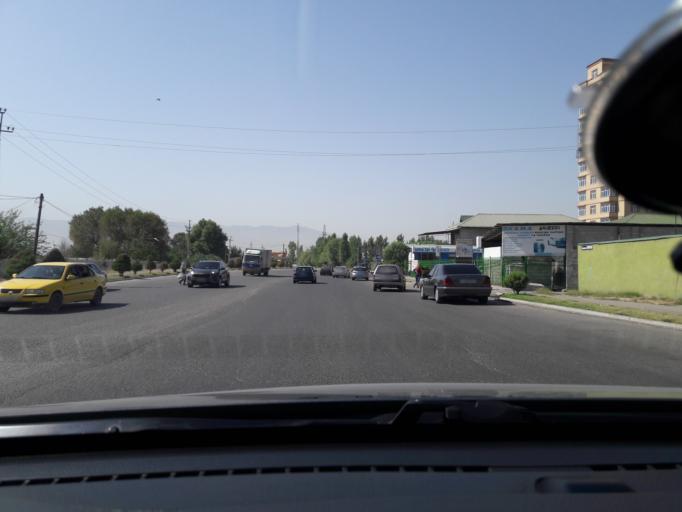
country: TJ
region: Dushanbe
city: Dushanbe
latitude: 38.5023
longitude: 68.7601
